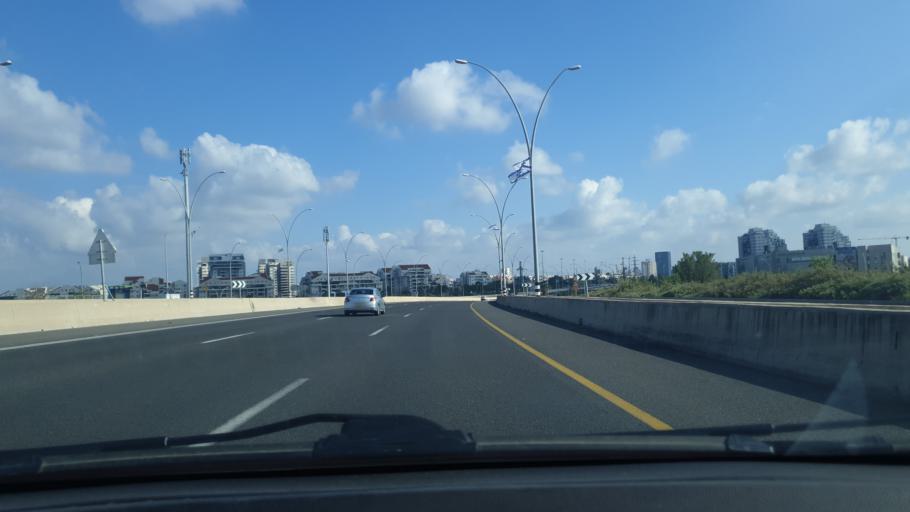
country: IL
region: Central District
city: Ra'anana
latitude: 32.1930
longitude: 34.8880
